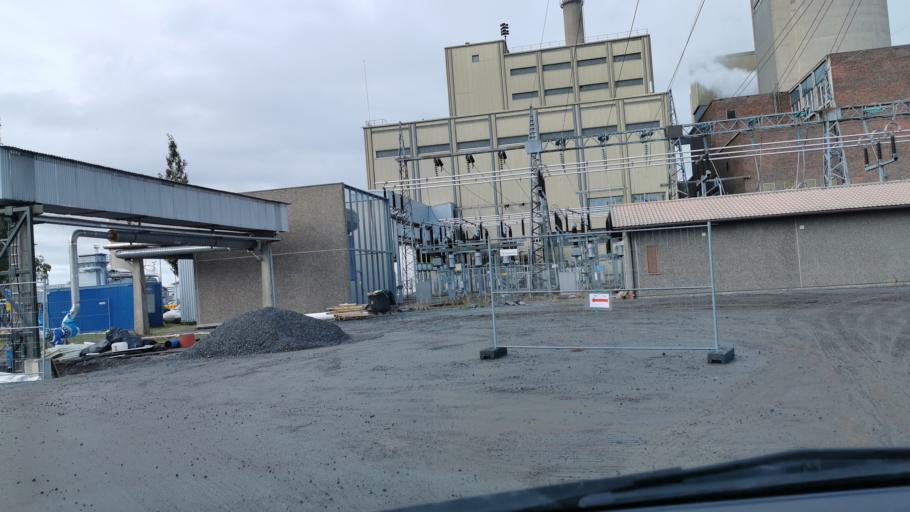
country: FI
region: Ostrobothnia
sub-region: Vaasa
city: Vaasa
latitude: 63.0911
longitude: 21.5575
